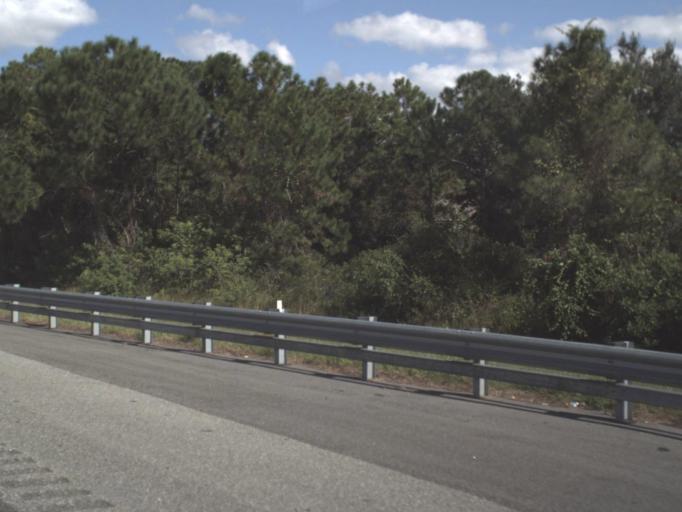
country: US
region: Florida
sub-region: Osceola County
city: Saint Cloud
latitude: 28.2045
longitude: -81.3067
